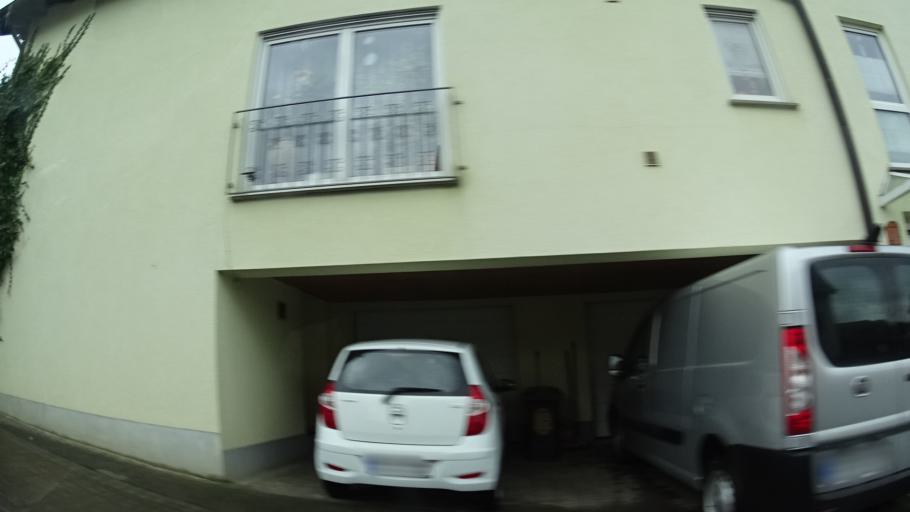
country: DE
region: Hesse
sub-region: Regierungsbezirk Kassel
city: Eichenzell
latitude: 50.4632
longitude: 9.6731
